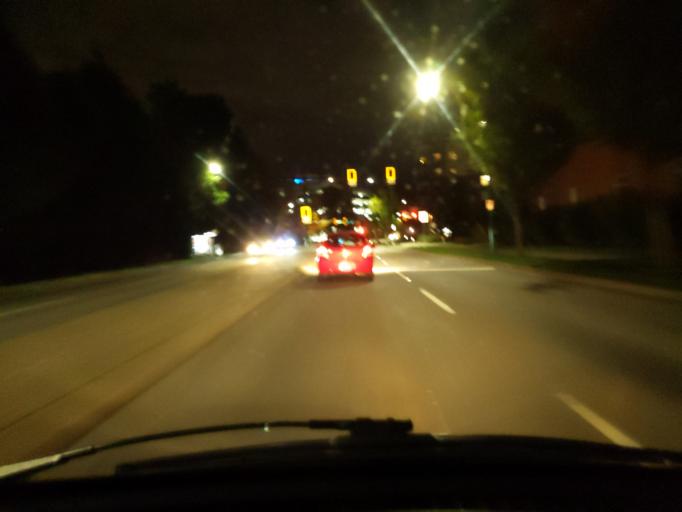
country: CA
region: British Columbia
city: Burnaby
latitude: 49.2560
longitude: -123.0116
